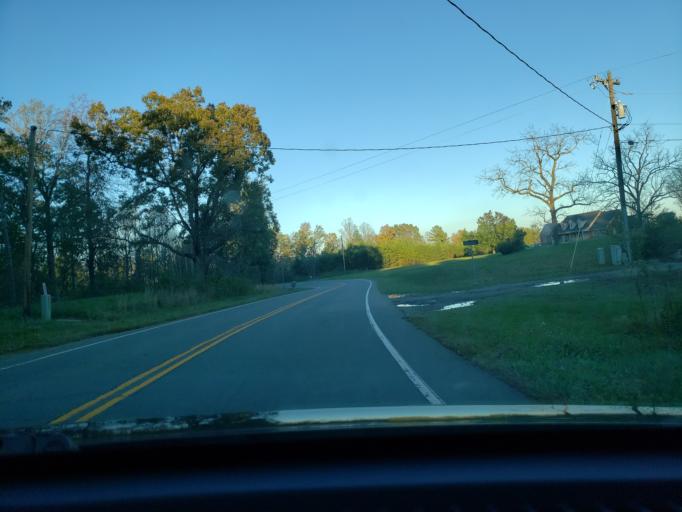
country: US
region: North Carolina
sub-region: Forsyth County
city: Rural Hall
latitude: 36.3149
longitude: -80.2376
